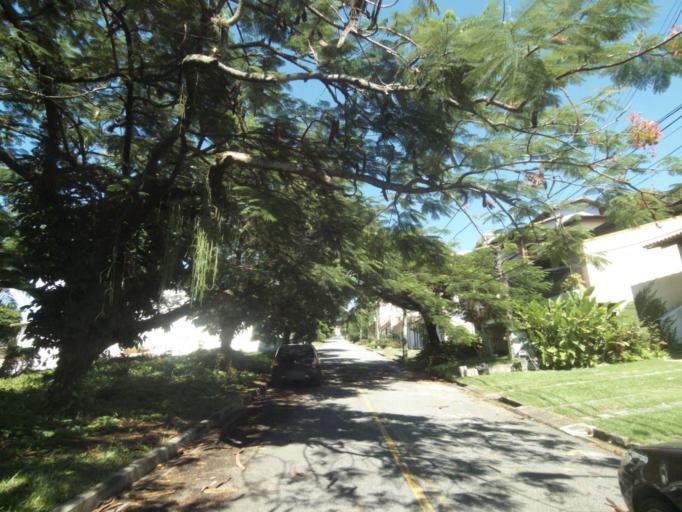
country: BR
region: Rio de Janeiro
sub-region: Niteroi
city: Niteroi
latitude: -22.9533
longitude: -43.0621
